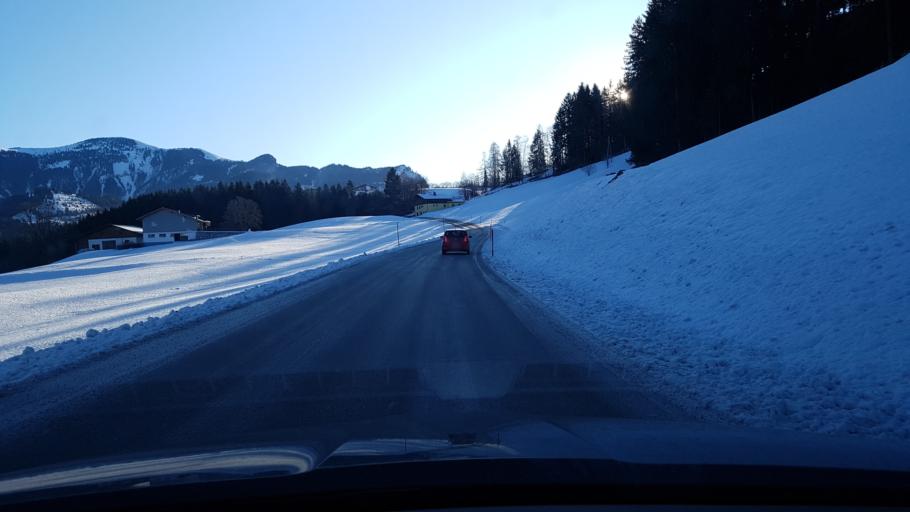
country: AT
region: Salzburg
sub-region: Politischer Bezirk Hallein
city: Kuchl
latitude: 47.6554
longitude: 13.1961
